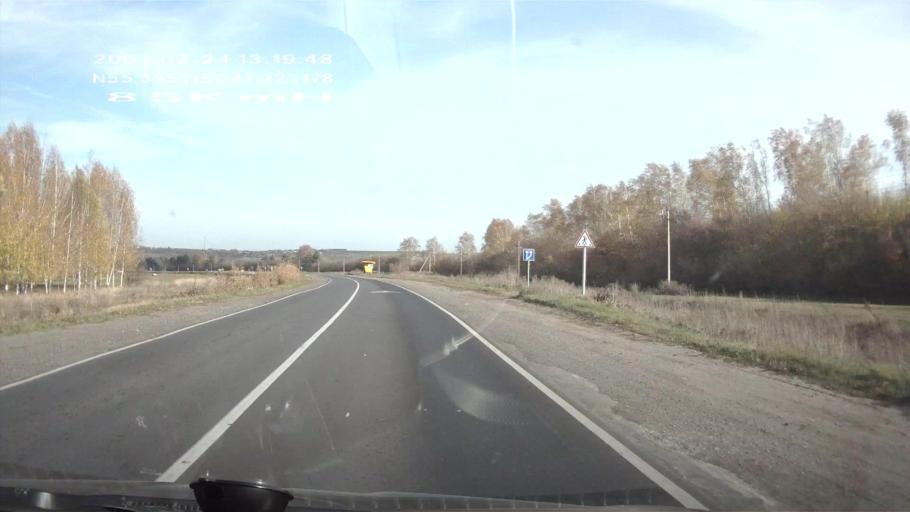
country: RU
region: Chuvashia
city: Ibresi
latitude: 55.3551
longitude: 47.2234
